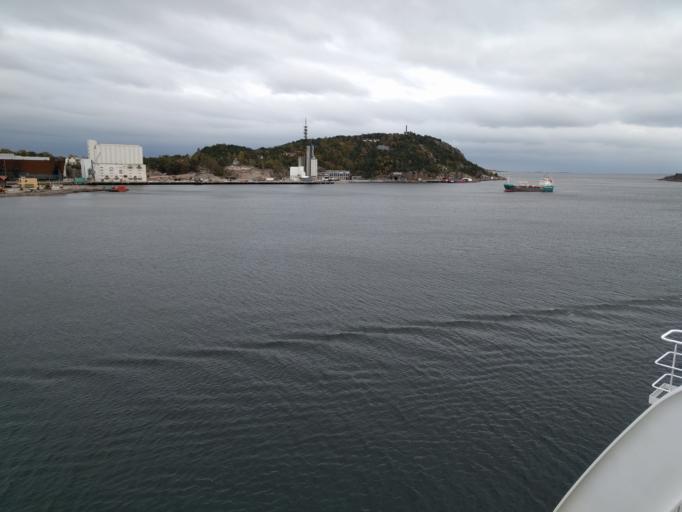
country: NO
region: Vest-Agder
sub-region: Kristiansand
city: Kristiansand
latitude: 58.1383
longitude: 7.9870
